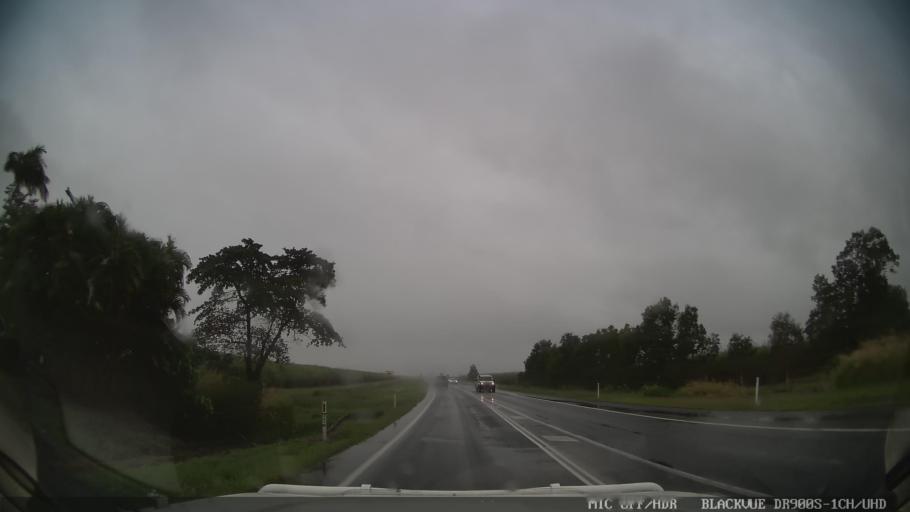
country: AU
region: Queensland
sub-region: Cassowary Coast
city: Innisfail
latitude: -17.7469
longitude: 146.0285
